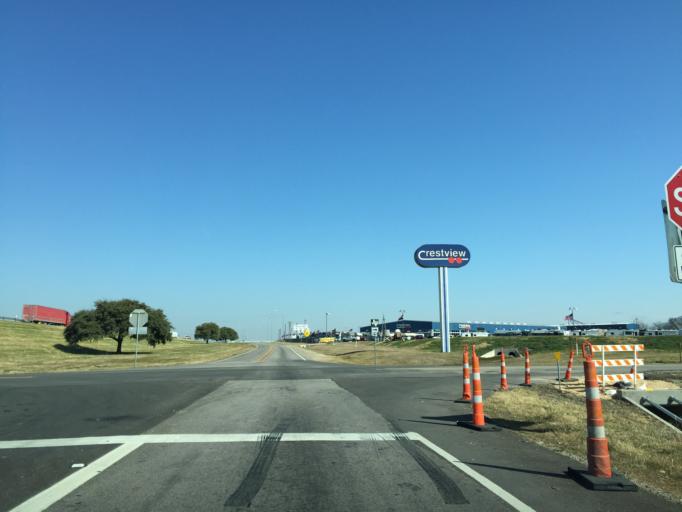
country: US
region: Texas
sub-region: Williamson County
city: Serenada
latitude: 30.7233
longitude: -97.6436
